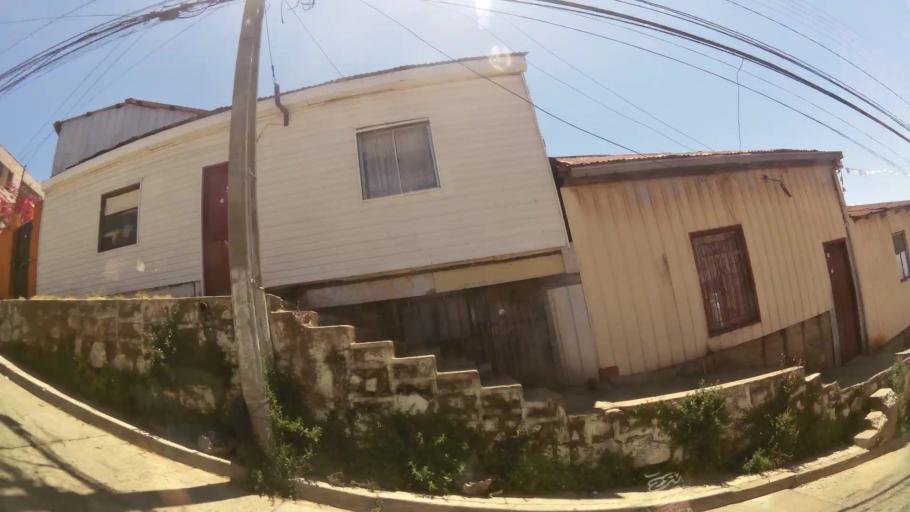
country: CL
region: Valparaiso
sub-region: Provincia de Valparaiso
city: Valparaiso
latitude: -33.0548
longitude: -71.6292
